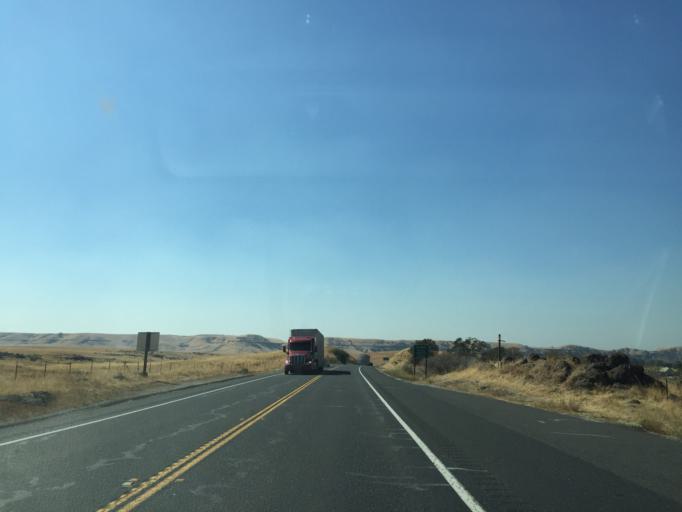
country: US
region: California
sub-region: Stanislaus County
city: East Oakdale
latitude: 37.8177
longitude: -120.6528
